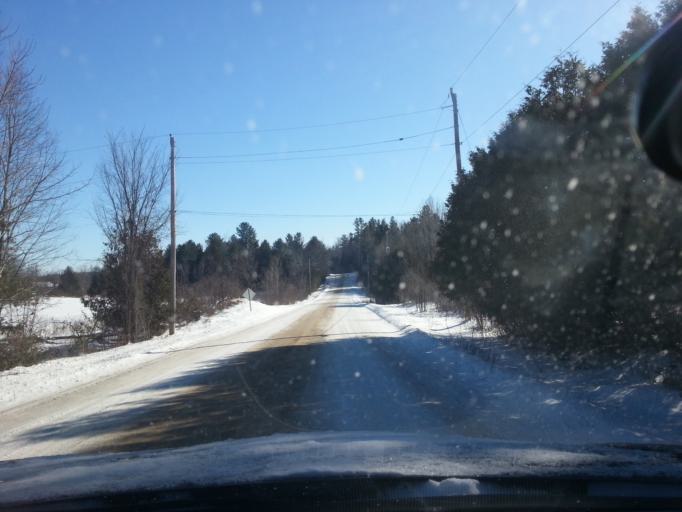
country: CA
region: Ontario
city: Arnprior
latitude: 45.2613
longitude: -76.3254
